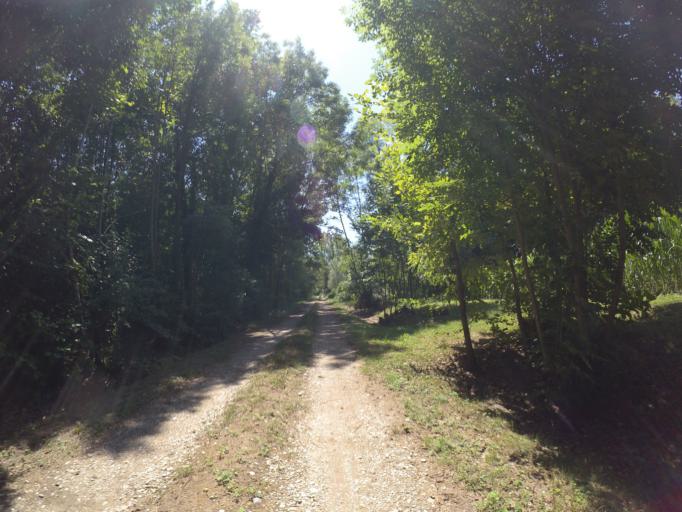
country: IT
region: Friuli Venezia Giulia
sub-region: Provincia di Udine
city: Bertiolo
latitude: 45.9244
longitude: 13.0810
